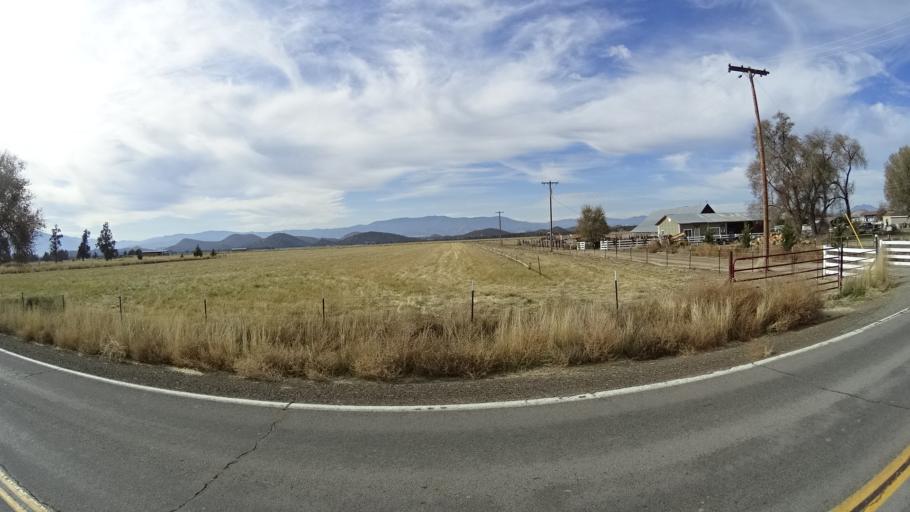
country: US
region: California
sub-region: Siskiyou County
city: Montague
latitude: 41.6141
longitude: -122.3996
